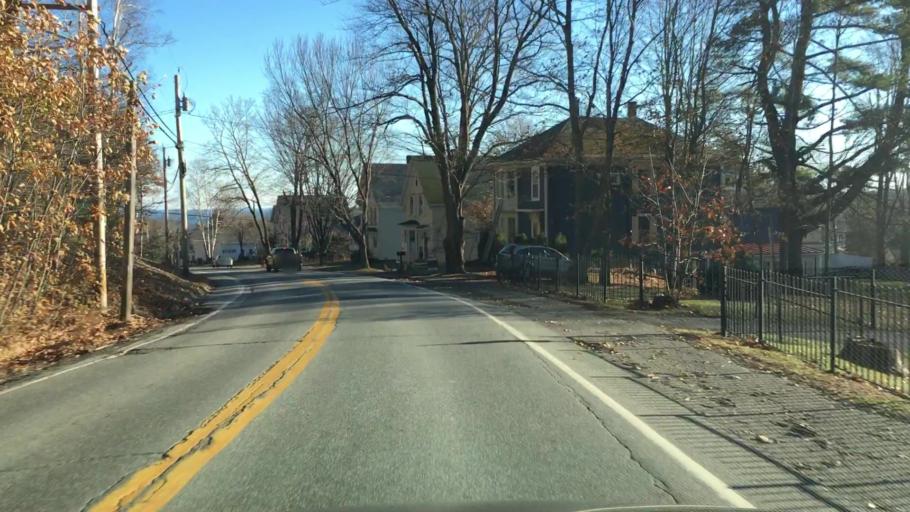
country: US
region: Maine
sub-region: Knox County
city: Camden
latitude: 44.2167
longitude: -69.0720
